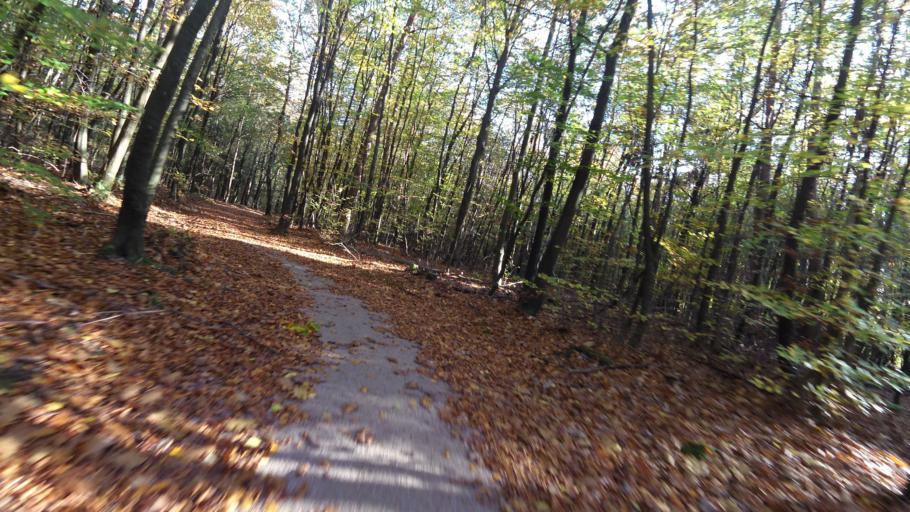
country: NL
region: Gelderland
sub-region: Gemeente Epe
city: Epe
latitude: 52.3659
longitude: 5.9657
